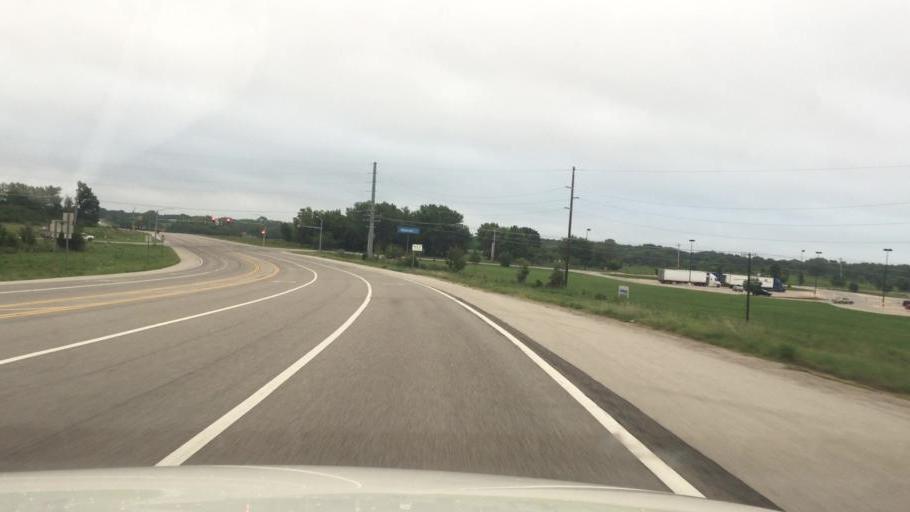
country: US
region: Kansas
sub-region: Montgomery County
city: Coffeyville
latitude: 37.0455
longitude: -95.5801
